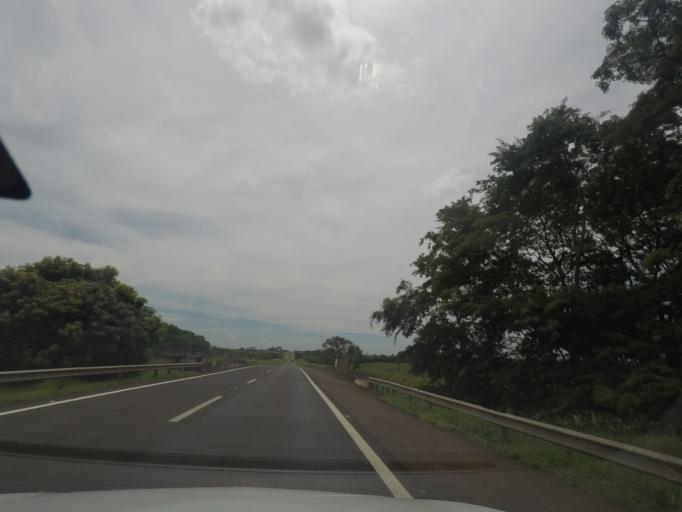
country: BR
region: Sao Paulo
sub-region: Bebedouro
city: Bebedouro
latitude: -20.9814
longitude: -48.4366
